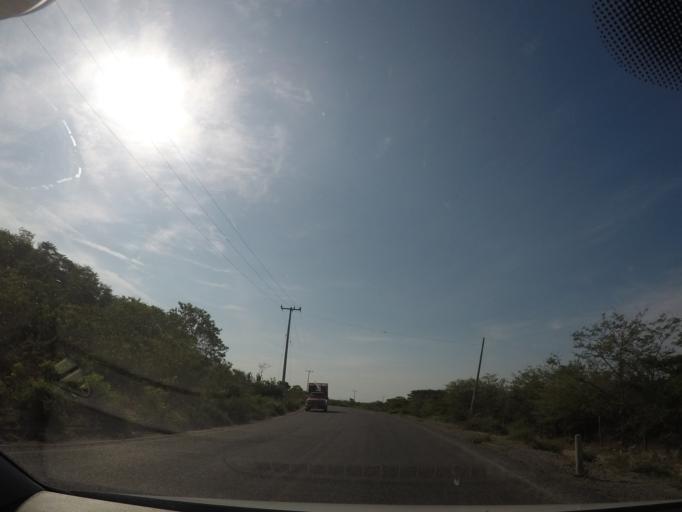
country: MX
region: Oaxaca
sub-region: Salina Cruz
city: Salina Cruz
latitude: 16.2289
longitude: -95.1400
